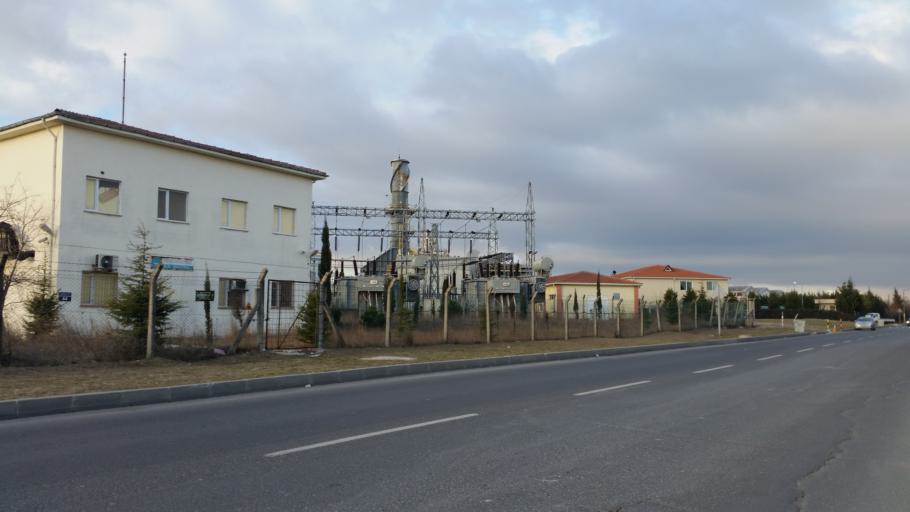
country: TR
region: Tekirdag
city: Cerkezkoey
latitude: 41.2916
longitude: 27.9568
